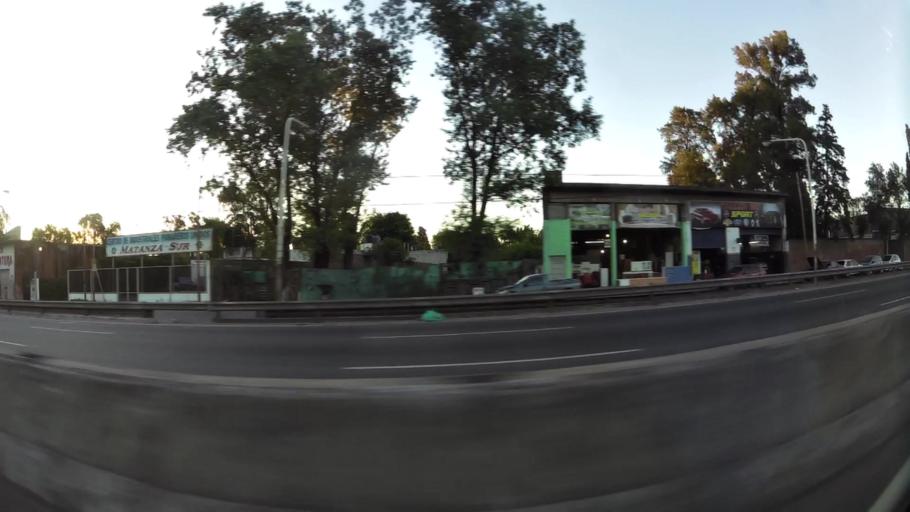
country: AR
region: Buenos Aires
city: Pontevedra
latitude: -34.7840
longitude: -58.6259
